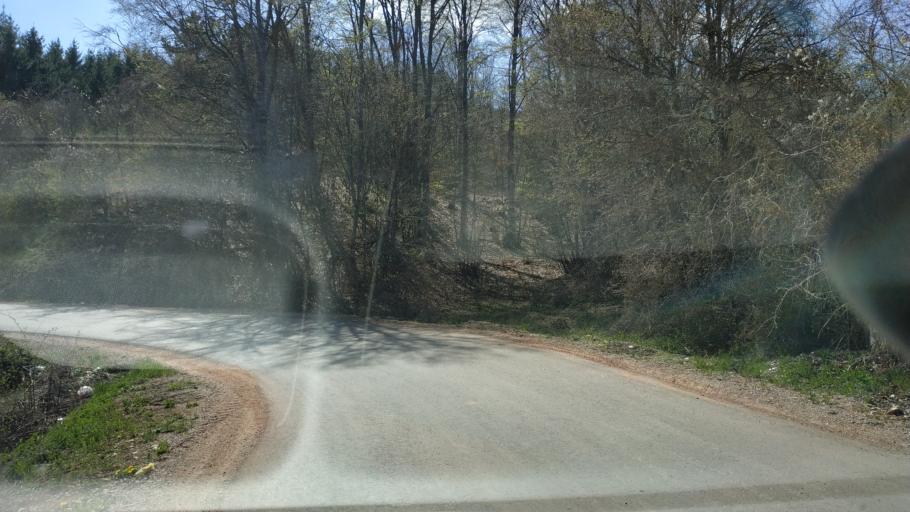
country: RS
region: Central Serbia
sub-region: Zajecarski Okrug
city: Soko Banja
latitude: 43.5817
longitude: 21.8928
